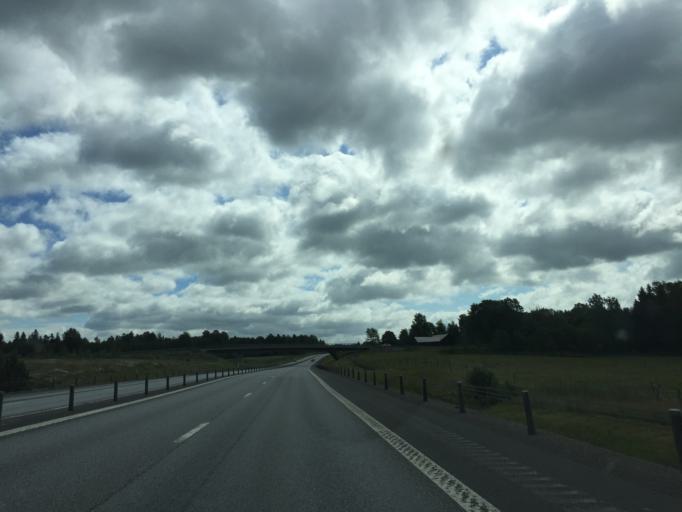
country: SE
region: OErebro
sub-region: Orebro Kommun
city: Vintrosa
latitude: 59.2538
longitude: 14.8985
